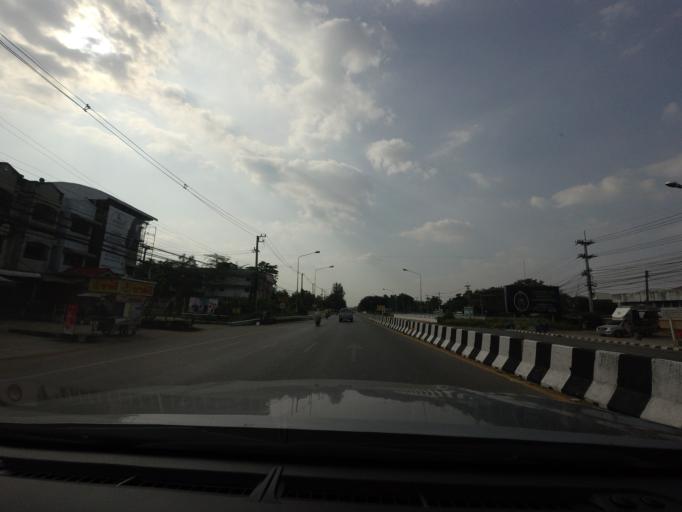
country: TH
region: Sukhothai
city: Sukhothai
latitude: 17.0099
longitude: 99.7954
